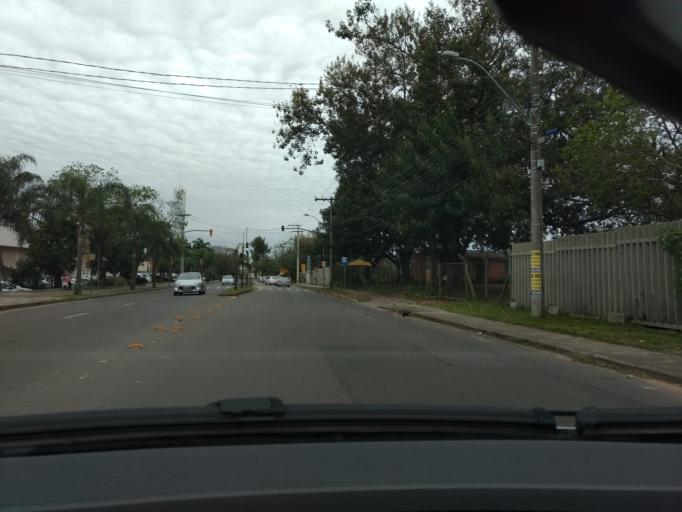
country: BR
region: Rio Grande do Sul
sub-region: Cachoeirinha
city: Cachoeirinha
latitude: -30.0286
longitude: -51.1323
